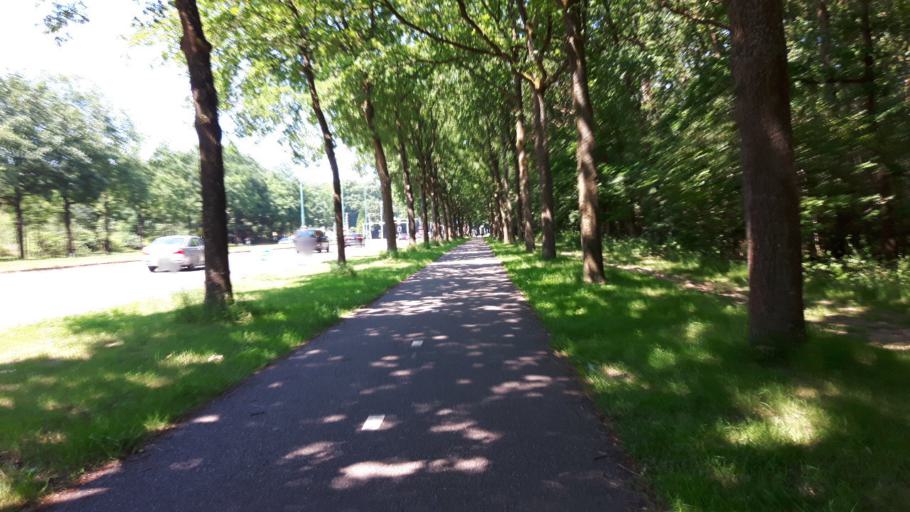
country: NL
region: Utrecht
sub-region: Gemeente Baarn
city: Baarn
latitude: 52.2011
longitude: 5.2765
